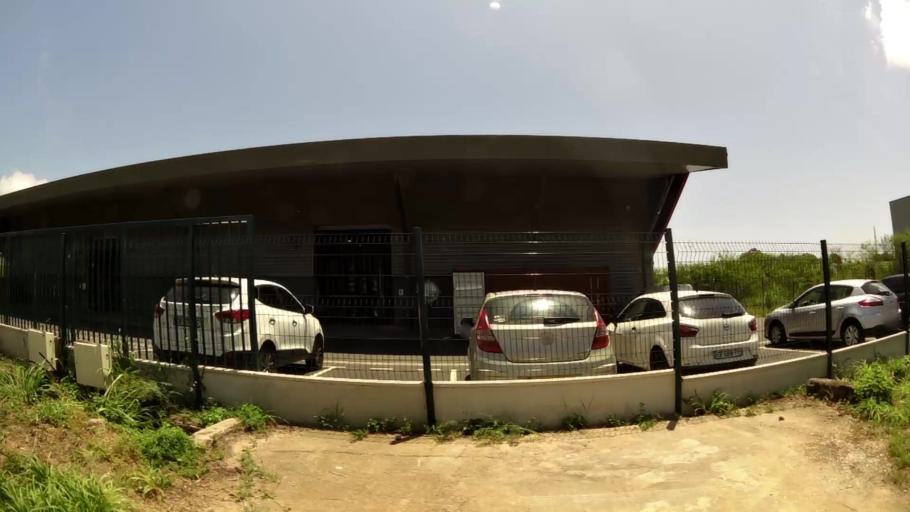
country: GF
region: Guyane
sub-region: Guyane
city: Cayenne
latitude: 4.9026
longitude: -52.3204
